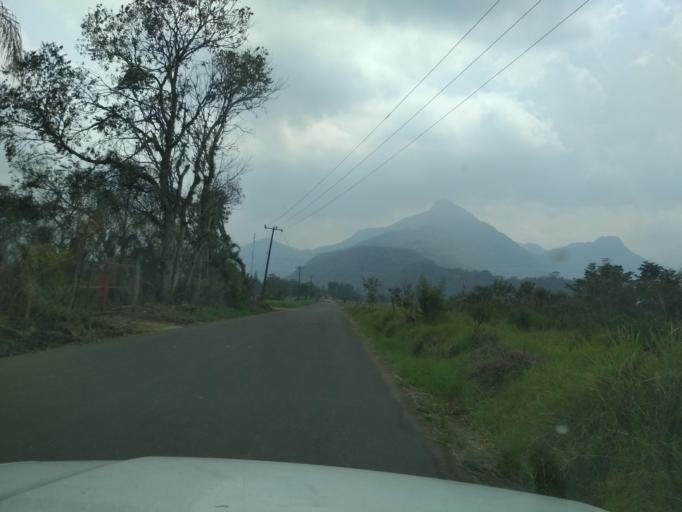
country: MX
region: Veracruz
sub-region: Cordoba
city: San Jose de Tapia
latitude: 18.8405
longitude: -96.9786
